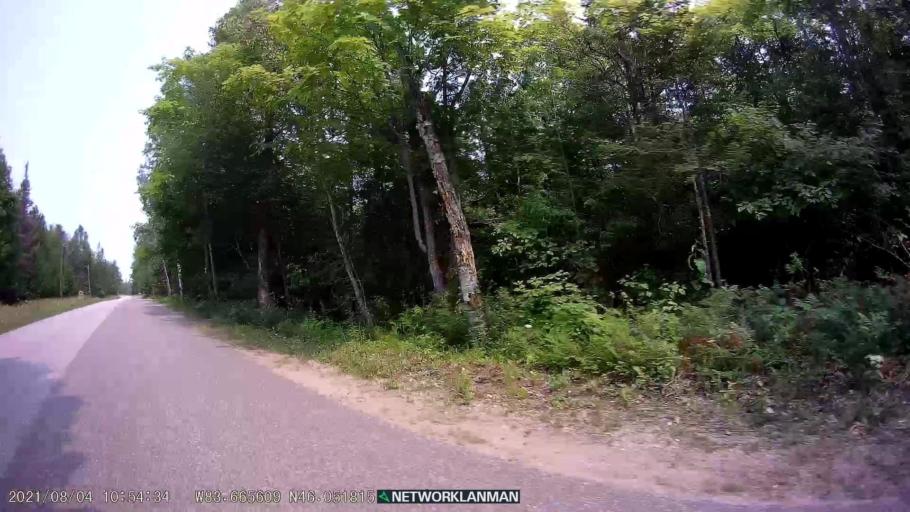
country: CA
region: Ontario
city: Thessalon
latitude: 46.0527
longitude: -83.6655
